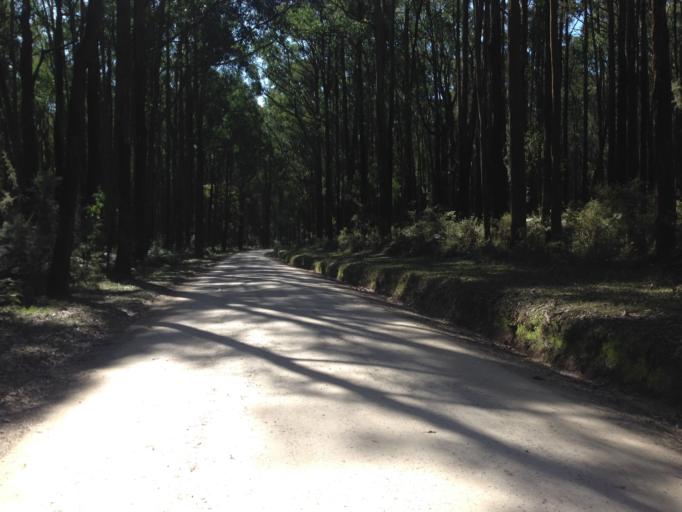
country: AU
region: Victoria
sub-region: Yarra Ranges
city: Mount Dandenong
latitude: -37.8351
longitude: 145.3975
